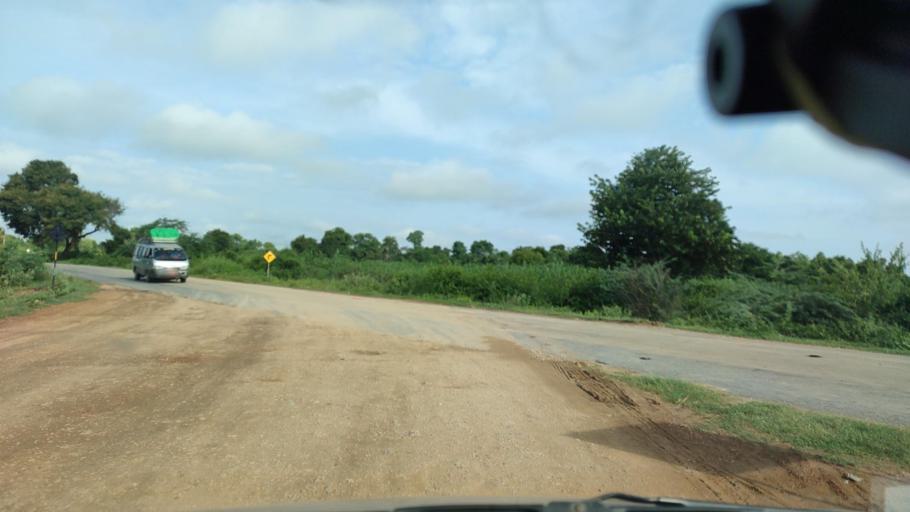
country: MM
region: Mandalay
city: Meiktila
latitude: 20.9463
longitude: 95.7728
